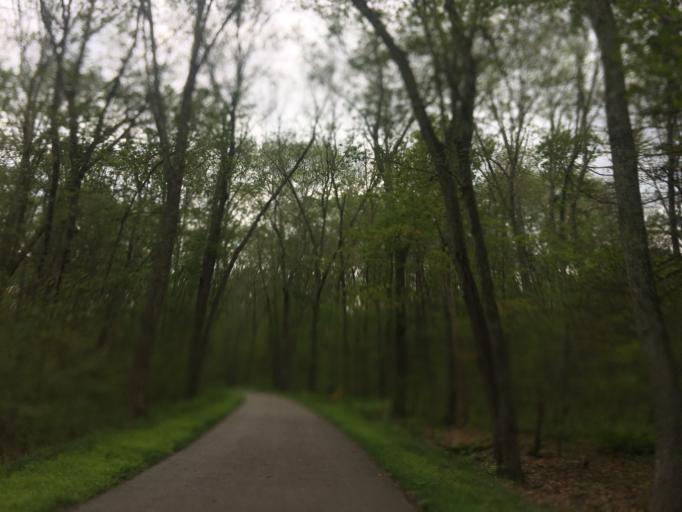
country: US
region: Connecticut
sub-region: Windham County
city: East Brooklyn
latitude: 41.7769
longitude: -71.9046
